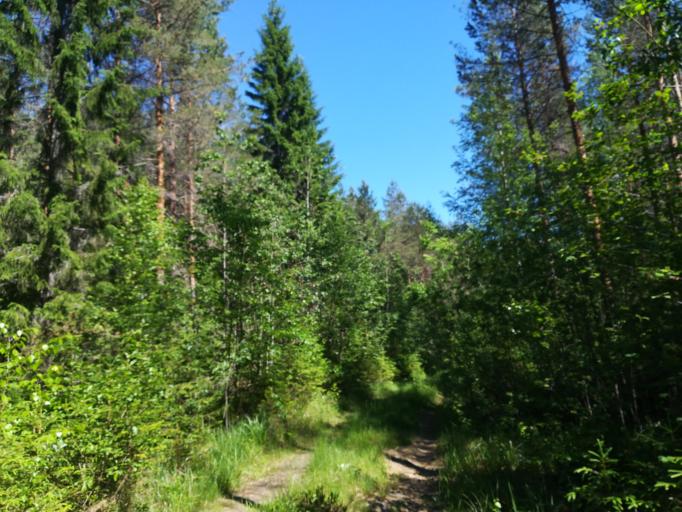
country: FI
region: Southern Savonia
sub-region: Mikkeli
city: Puumala
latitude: 61.6160
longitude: 28.1651
